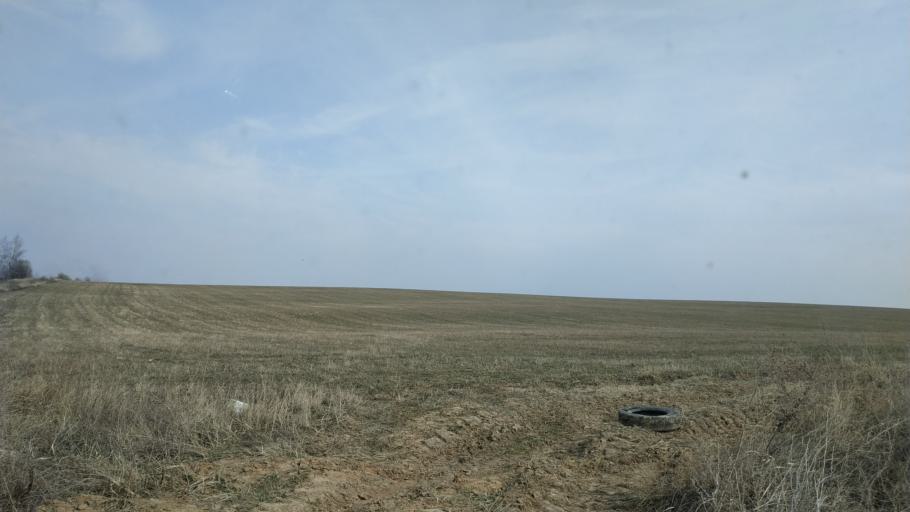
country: RU
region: Moskovskaya
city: Troitskoye
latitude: 55.3579
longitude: 38.4644
